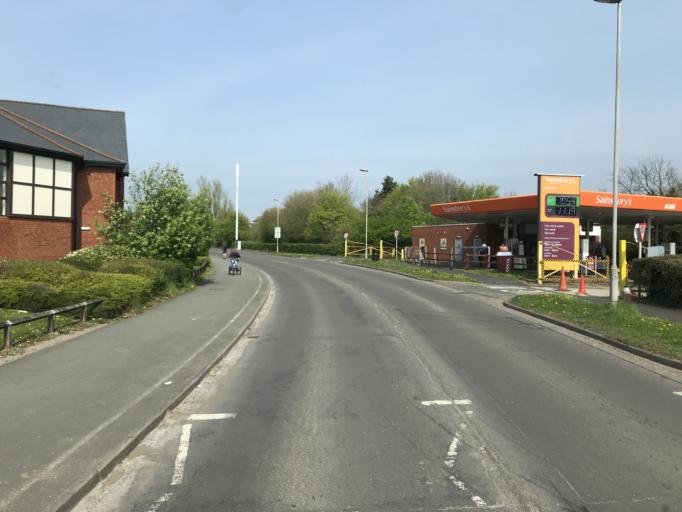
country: GB
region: England
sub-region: Cheshire West and Chester
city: Hoole
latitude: 53.1844
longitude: -2.8559
